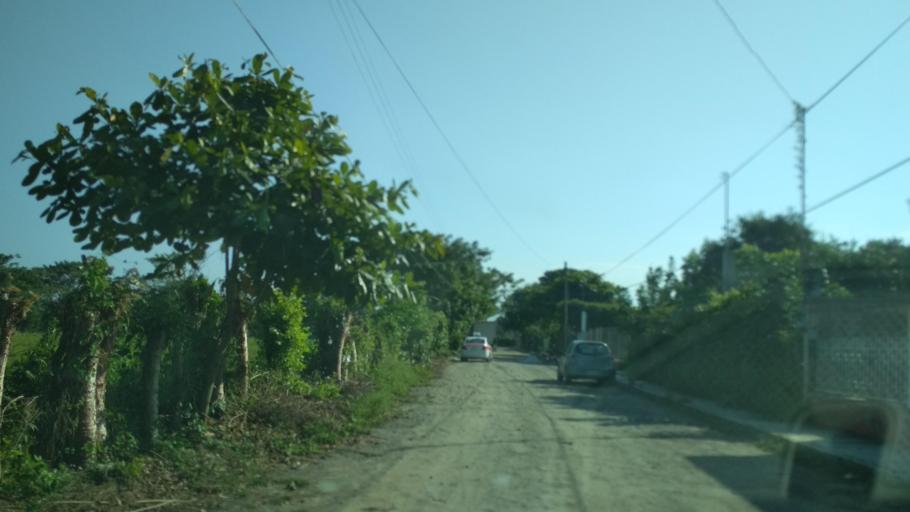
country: MX
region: Veracruz
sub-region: Martinez de la Torre
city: El Progreso
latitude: 20.0833
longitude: -97.0219
